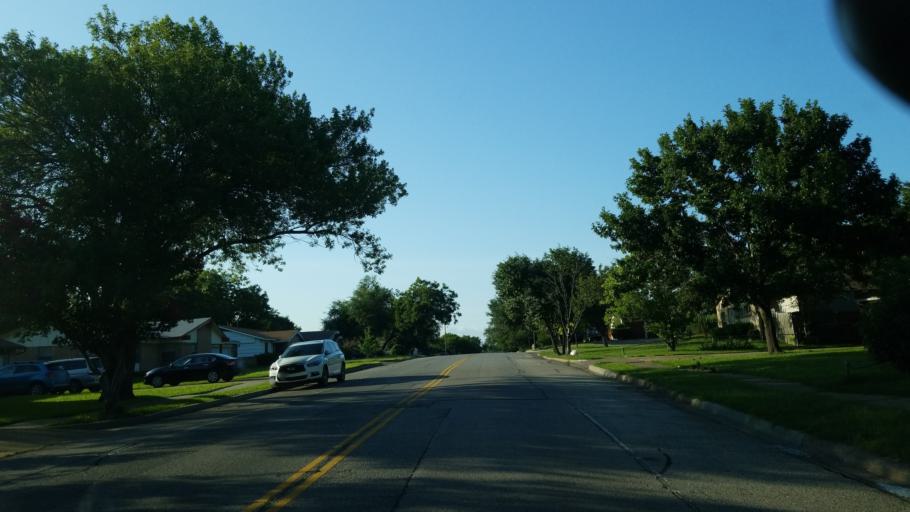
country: US
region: Texas
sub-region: Dallas County
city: Carrollton
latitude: 32.9416
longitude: -96.8834
